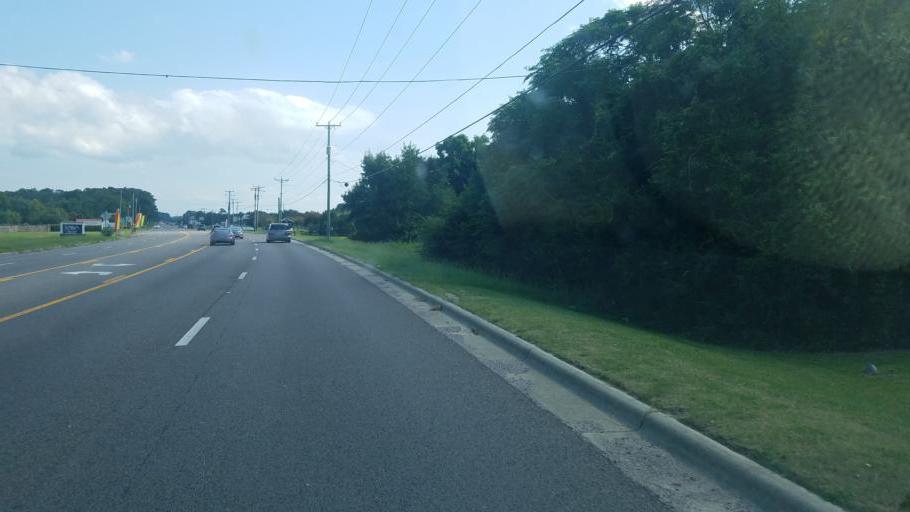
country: US
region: North Carolina
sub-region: Dare County
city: Southern Shores
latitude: 36.2304
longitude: -75.8735
